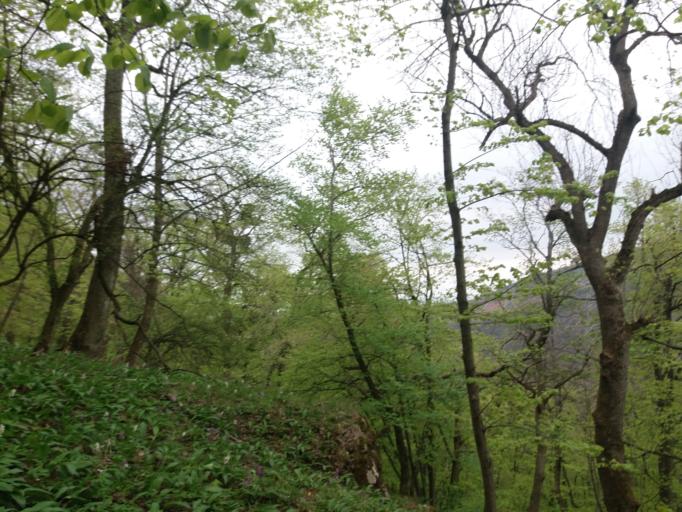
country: HU
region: Komarom-Esztergom
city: Labatlan
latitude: 47.6873
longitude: 18.5020
